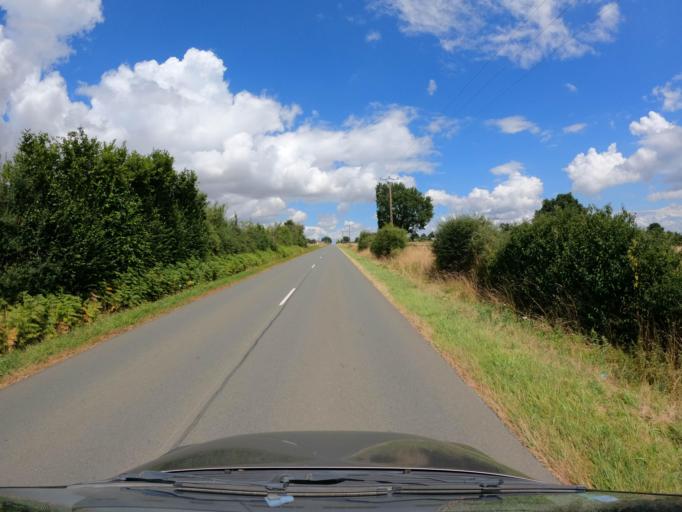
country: FR
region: Pays de la Loire
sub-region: Departement de Maine-et-Loire
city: Chateauneuf-sur-Sarthe
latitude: 47.7160
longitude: -0.5290
